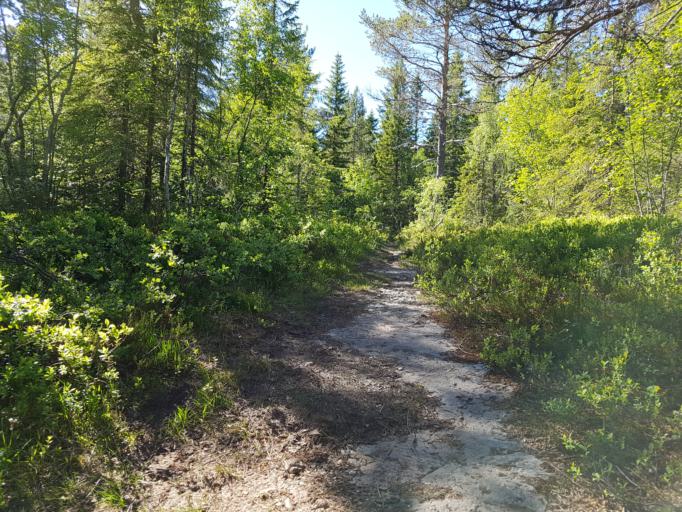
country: NO
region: Sor-Trondelag
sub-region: Trondheim
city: Trondheim
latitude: 63.4075
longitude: 10.3169
